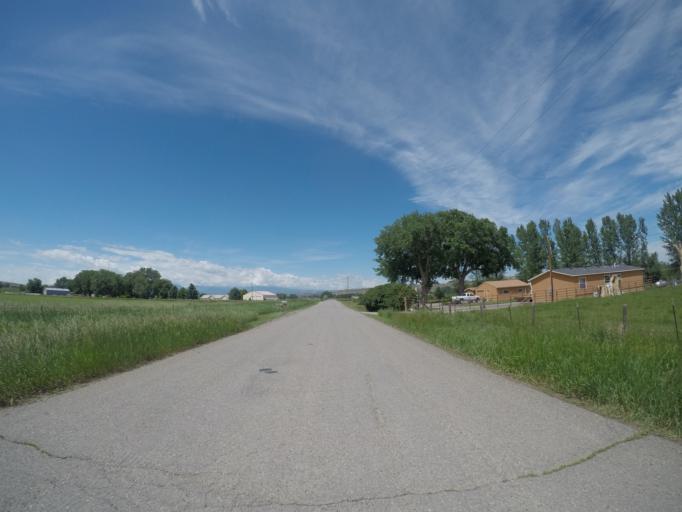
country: US
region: Montana
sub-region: Carbon County
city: Red Lodge
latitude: 45.2577
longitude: -108.8935
